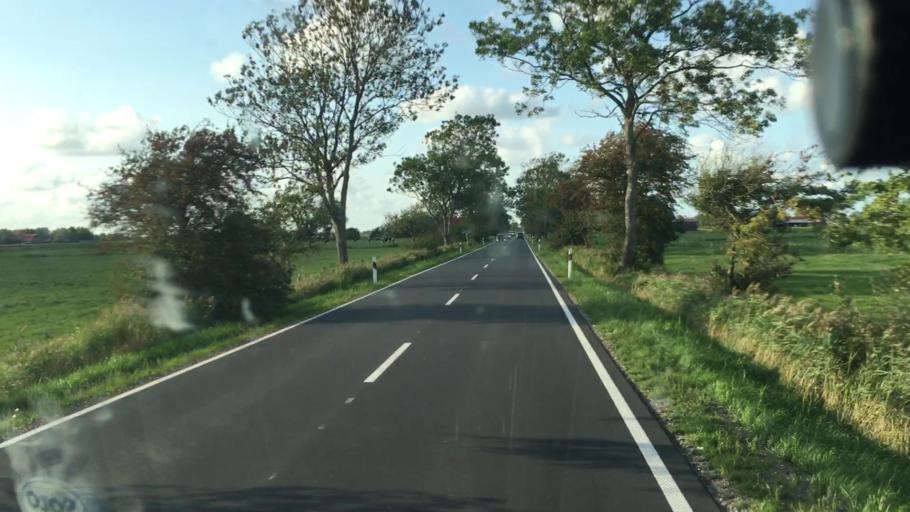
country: DE
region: Lower Saxony
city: Jever
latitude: 53.6177
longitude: 7.8657
